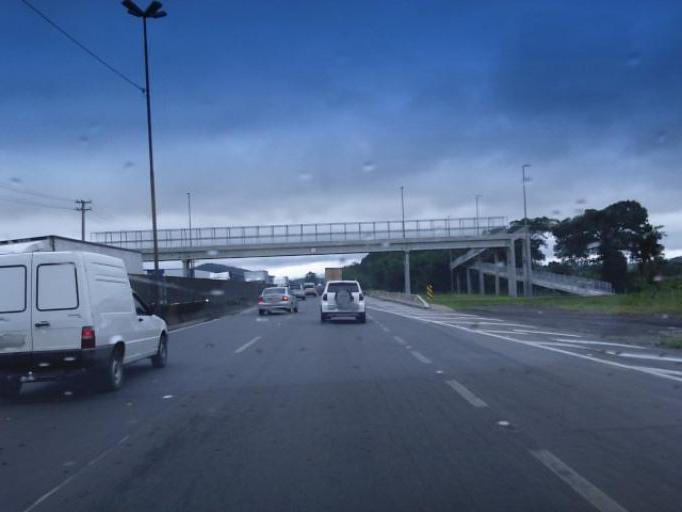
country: BR
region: Santa Catarina
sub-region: Itajai
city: Itajai
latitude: -26.9215
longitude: -48.7083
